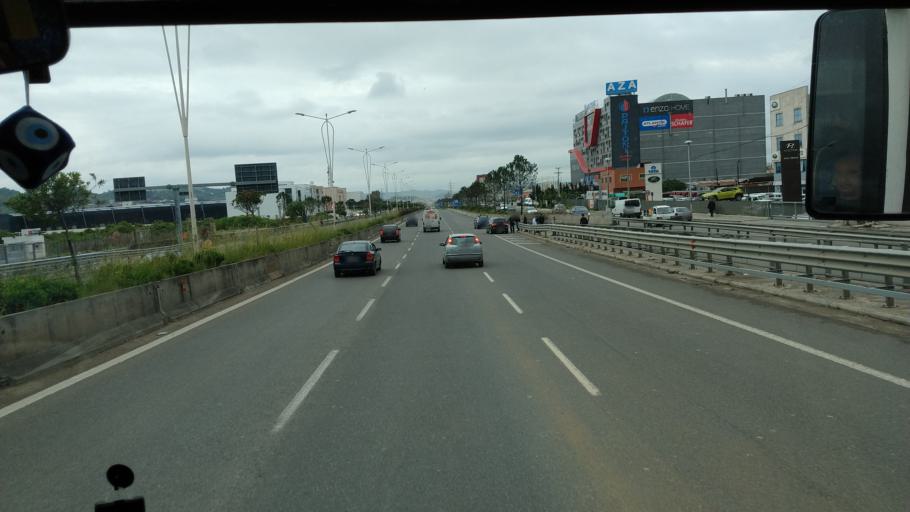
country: AL
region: Tirane
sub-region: Rrethi i Tiranes
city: Paskuqan
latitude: 41.3442
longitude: 19.7727
